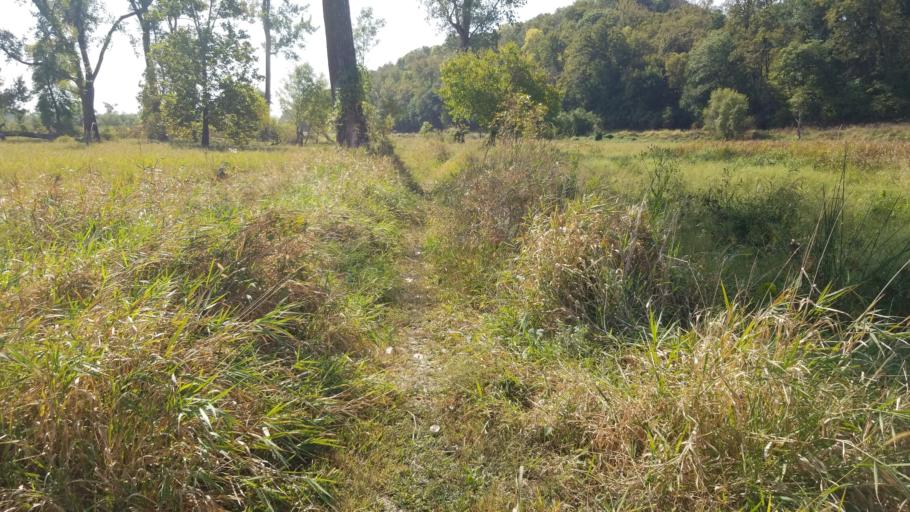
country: US
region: Nebraska
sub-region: Sarpy County
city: Bellevue
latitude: 41.1717
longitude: -95.8908
